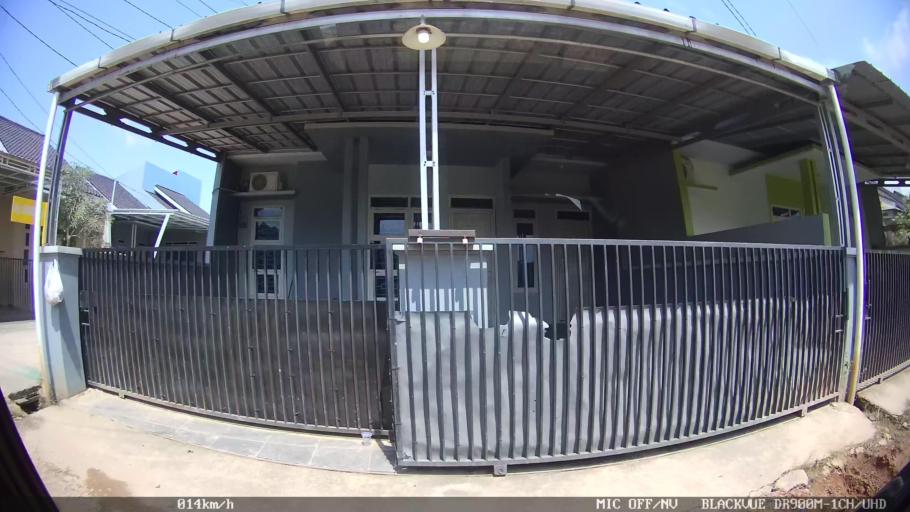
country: ID
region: Lampung
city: Kedaton
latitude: -5.3511
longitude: 105.2834
